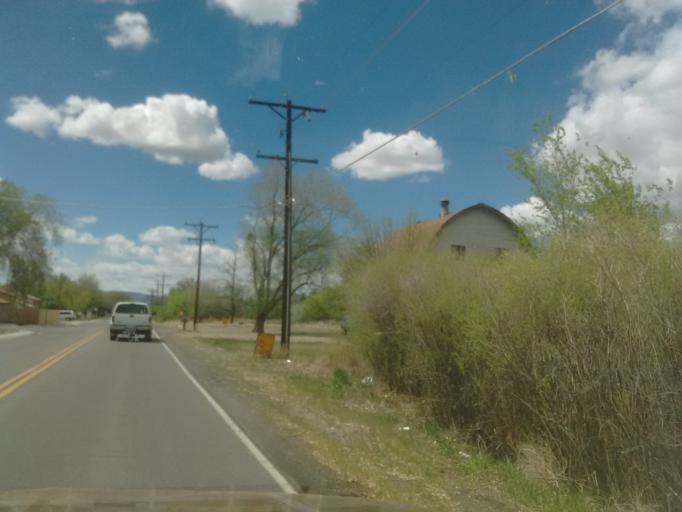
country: US
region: Colorado
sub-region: Mesa County
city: Fruitvale
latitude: 39.0774
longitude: -108.4869
